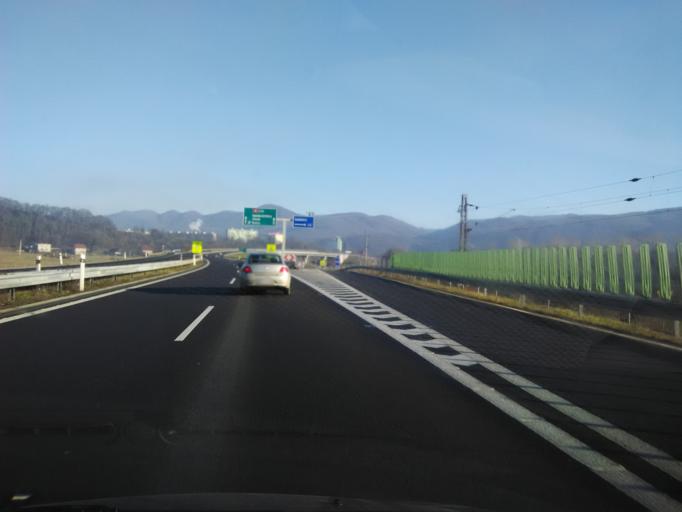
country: SK
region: Banskobystricky
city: Zarnovica
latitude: 48.4716
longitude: 18.7079
